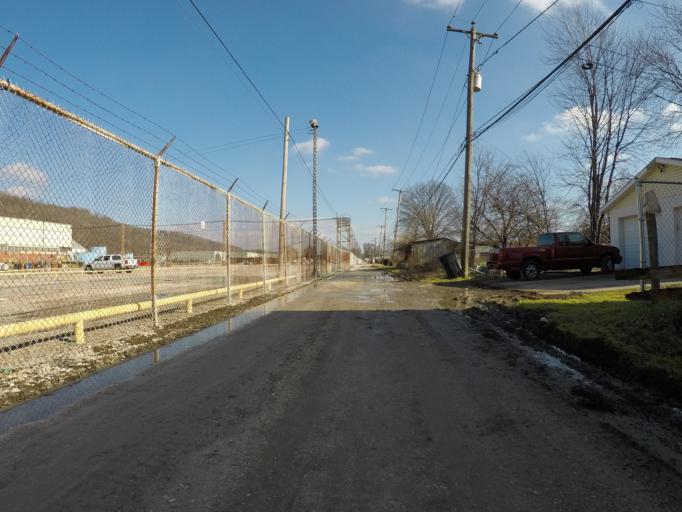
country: US
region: West Virginia
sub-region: Cabell County
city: Pea Ridge
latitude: 38.4142
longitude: -82.3796
